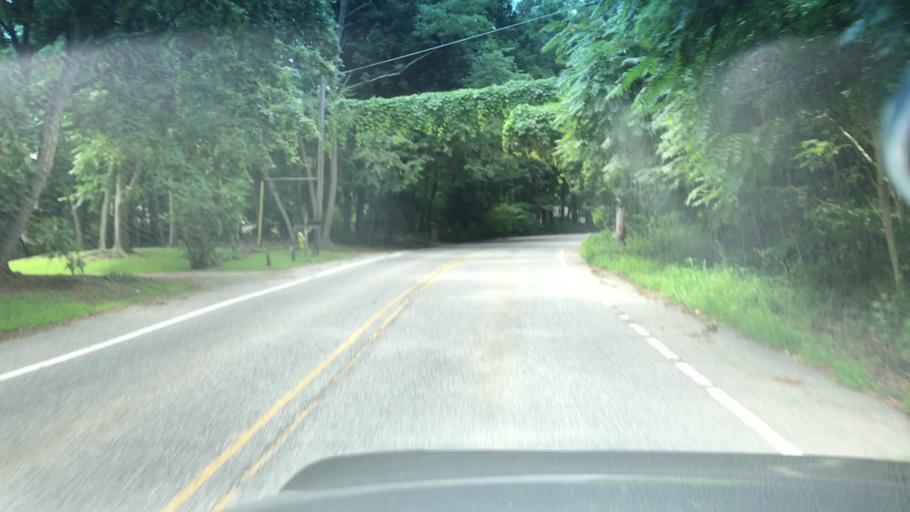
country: US
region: New York
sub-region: Suffolk County
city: Wading River
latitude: 40.9535
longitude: -72.8535
